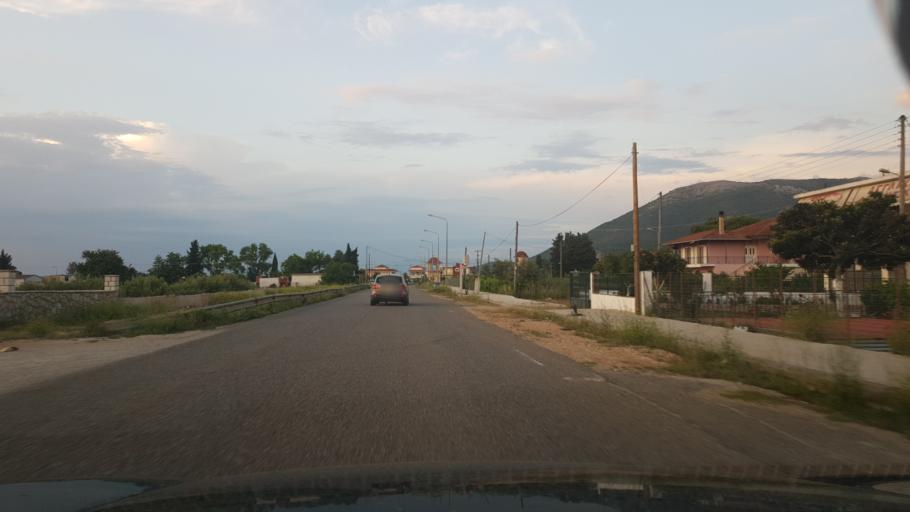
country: GR
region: West Greece
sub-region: Nomos Aitolias kai Akarnanias
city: Vonitsa
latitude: 38.9081
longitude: 20.8848
